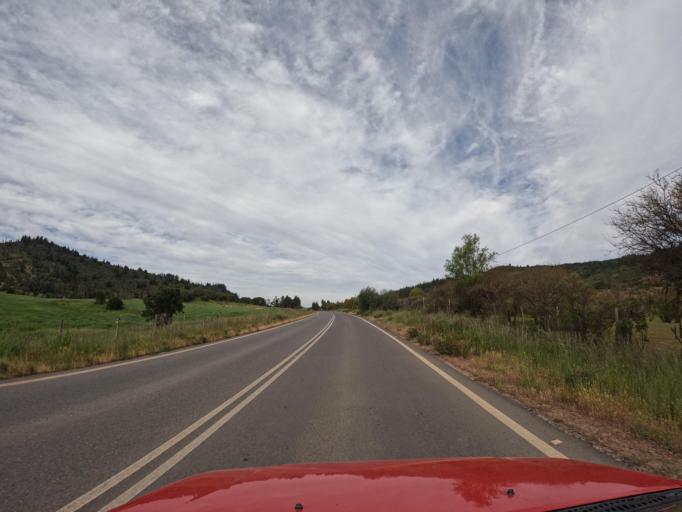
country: CL
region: Maule
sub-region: Provincia de Talca
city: Talca
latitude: -35.3229
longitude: -71.9501
